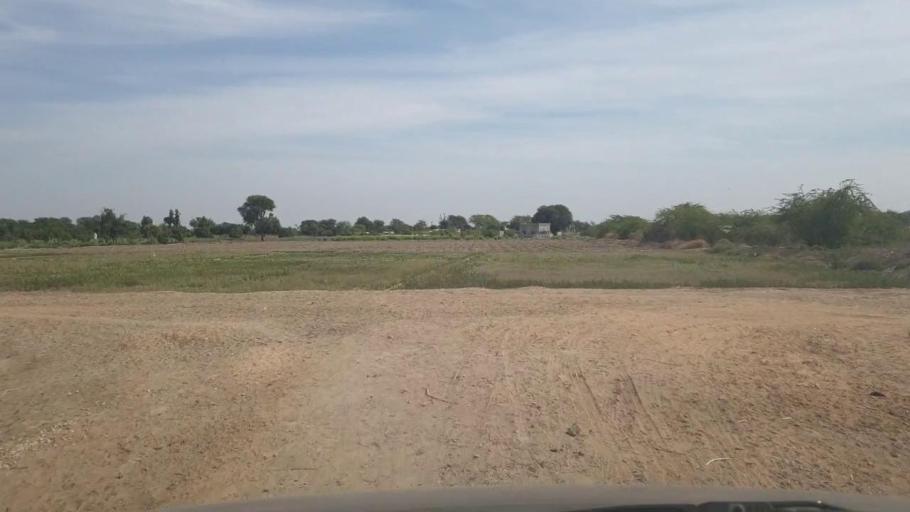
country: PK
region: Sindh
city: Kunri
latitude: 25.2379
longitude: 69.6446
